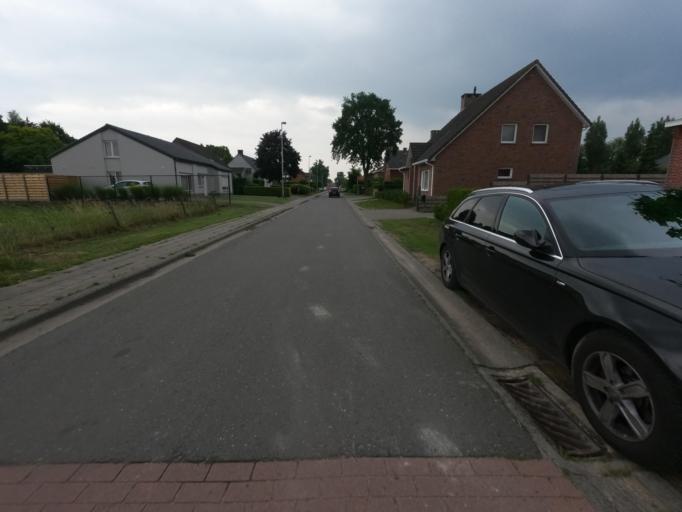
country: BE
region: Flanders
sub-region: Provincie Antwerpen
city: Essen
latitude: 51.4690
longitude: 4.4930
